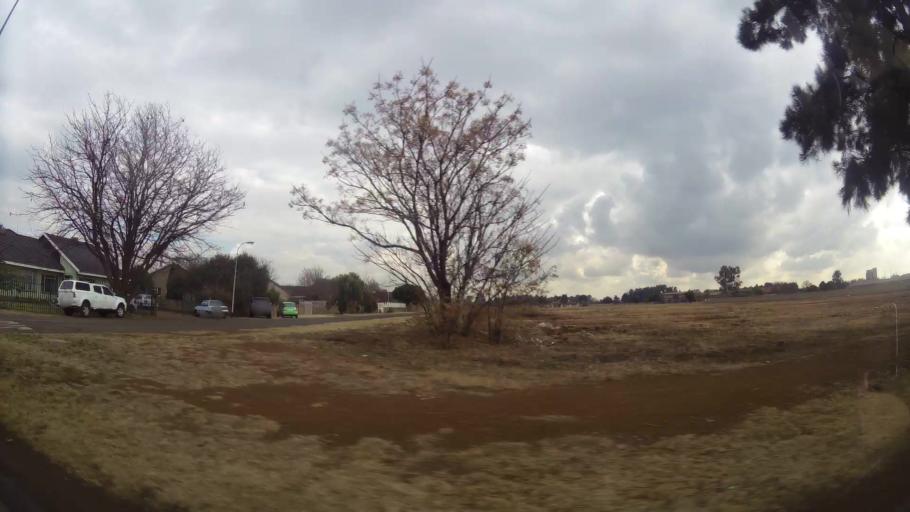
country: ZA
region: Gauteng
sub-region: Sedibeng District Municipality
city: Meyerton
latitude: -26.5780
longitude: 28.0056
